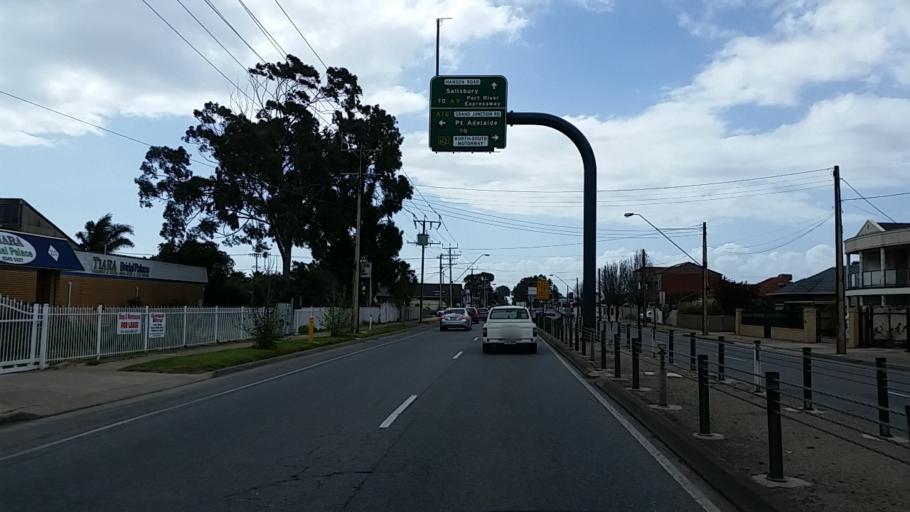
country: AU
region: South Australia
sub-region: Charles Sturt
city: Woodville North
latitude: -34.8534
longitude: 138.5469
